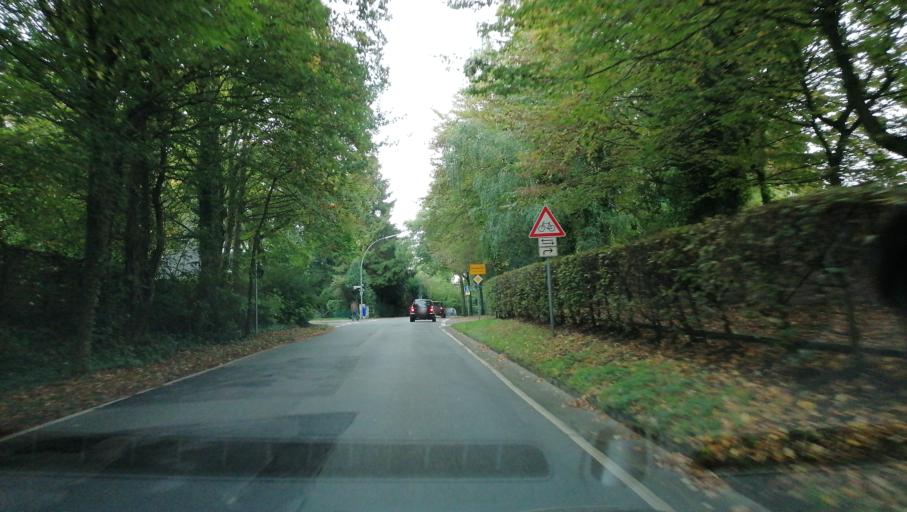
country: DE
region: North Rhine-Westphalia
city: Herten
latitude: 51.5734
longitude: 7.1077
